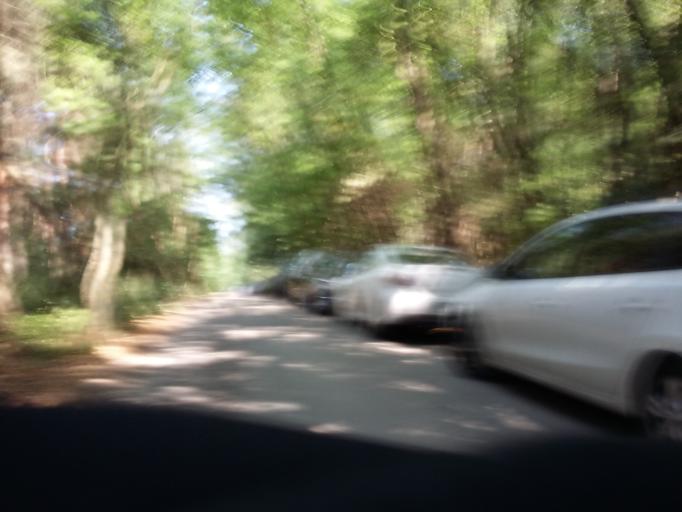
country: SK
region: Bratislavsky
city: Stupava
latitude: 48.3069
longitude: 17.0427
